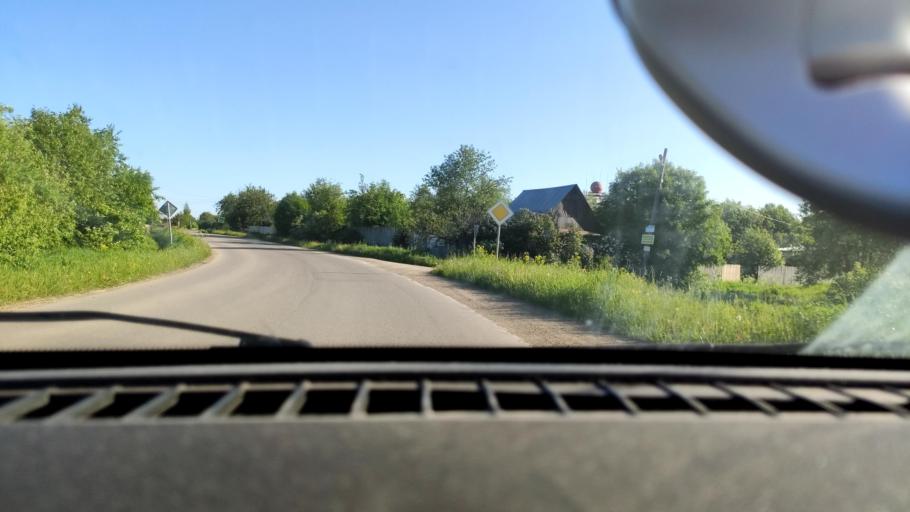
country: RU
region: Perm
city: Polazna
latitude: 58.2041
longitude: 56.4992
